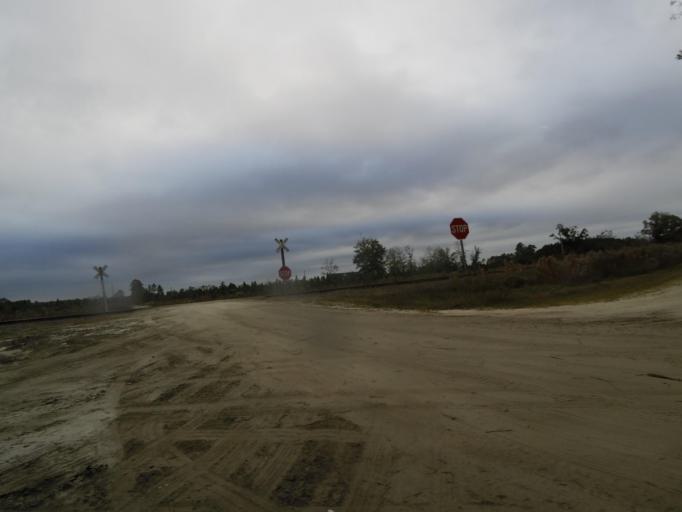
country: US
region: Georgia
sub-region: Charlton County
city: Folkston
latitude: 30.8996
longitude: -82.0685
